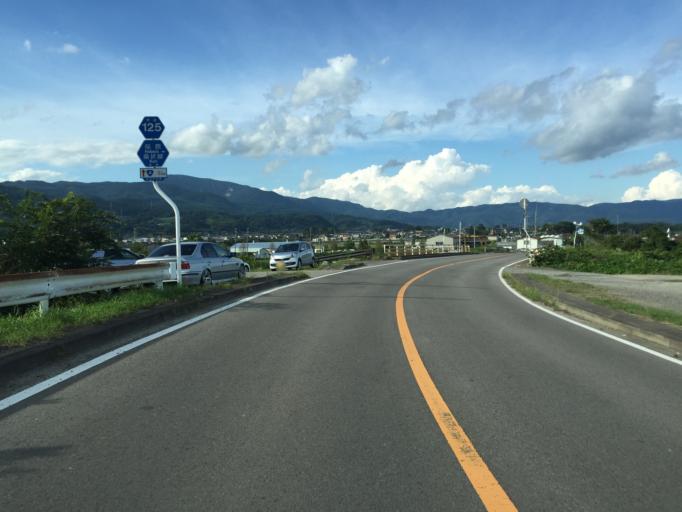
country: JP
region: Fukushima
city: Hobaramachi
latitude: 37.8308
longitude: 140.5179
